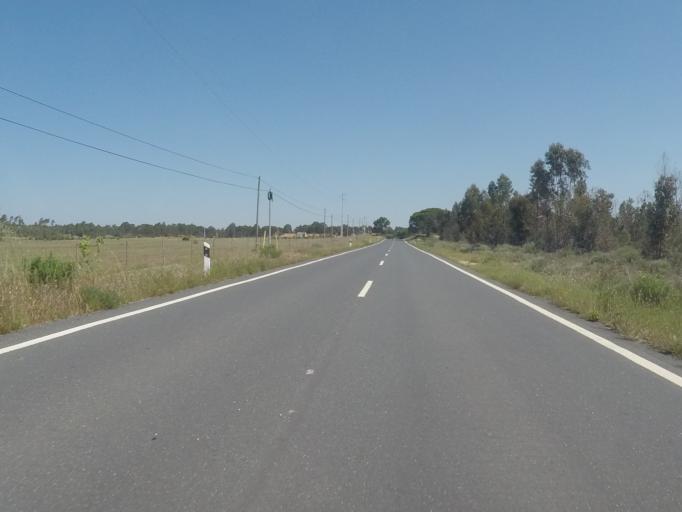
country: PT
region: Setubal
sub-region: Grandola
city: Grandola
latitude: 38.2490
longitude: -8.7375
